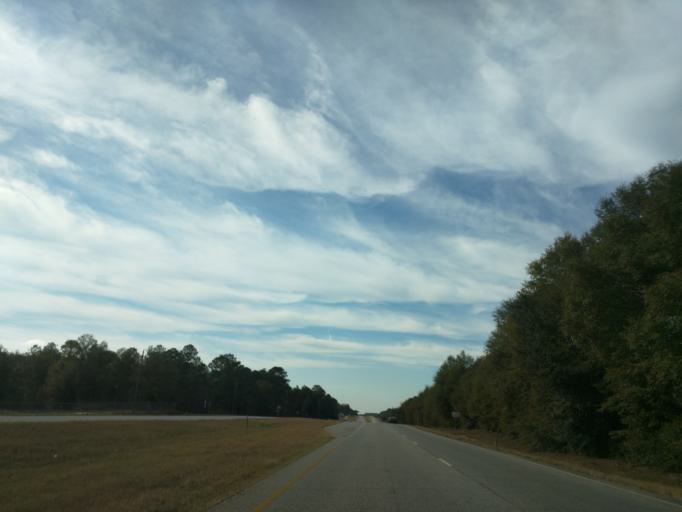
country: US
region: Georgia
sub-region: Decatur County
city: Bainbridge
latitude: 30.8963
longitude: -84.5076
